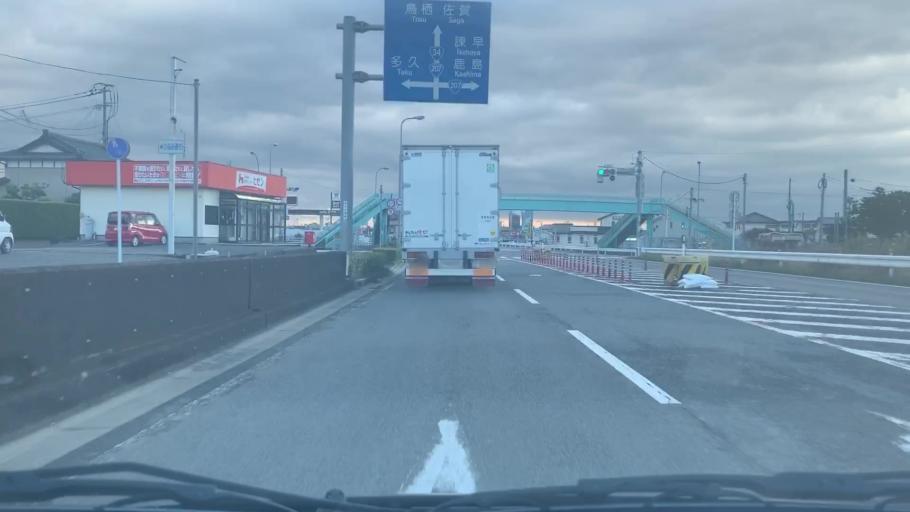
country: JP
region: Saga Prefecture
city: Kashima
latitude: 33.2181
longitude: 130.1562
